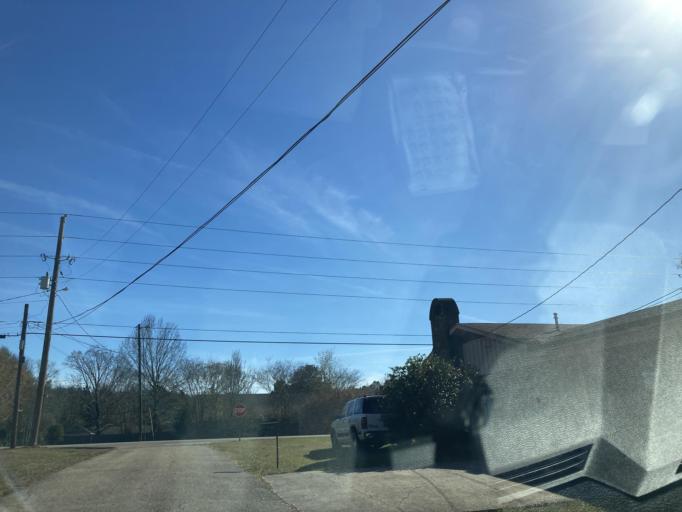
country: US
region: Mississippi
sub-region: Forrest County
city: Petal
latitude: 31.3346
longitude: -89.2461
